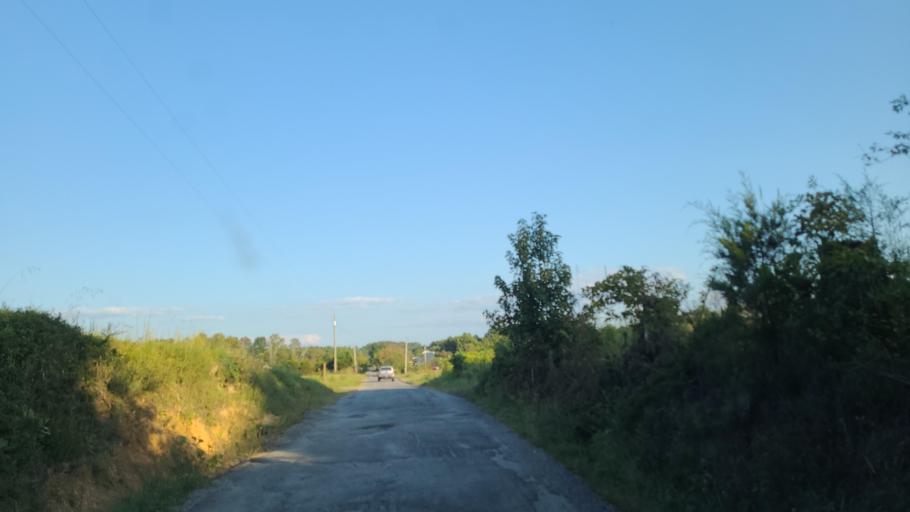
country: US
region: Tennessee
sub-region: Bradley County
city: Wildwood Lake
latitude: 35.0186
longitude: -84.7594
